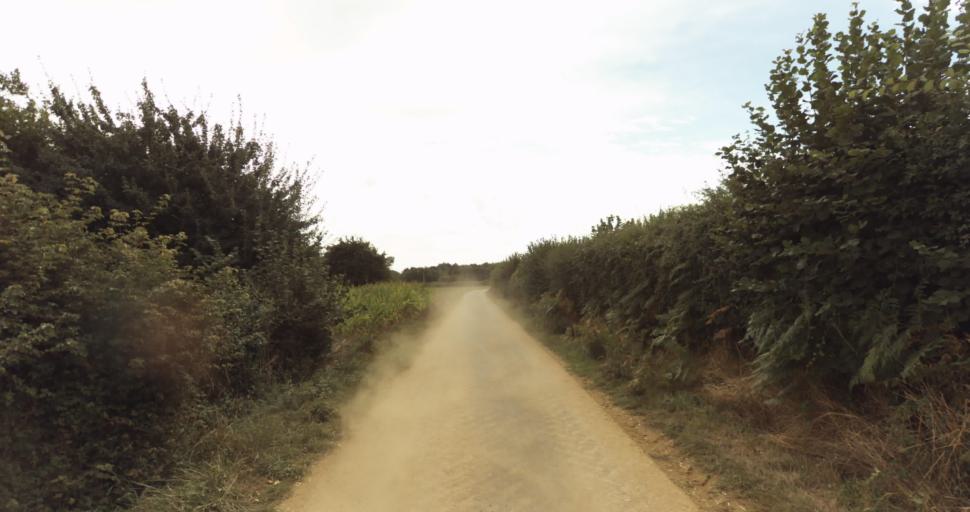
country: FR
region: Lower Normandy
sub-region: Departement de l'Orne
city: Vimoutiers
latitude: 48.9527
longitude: 0.3102
